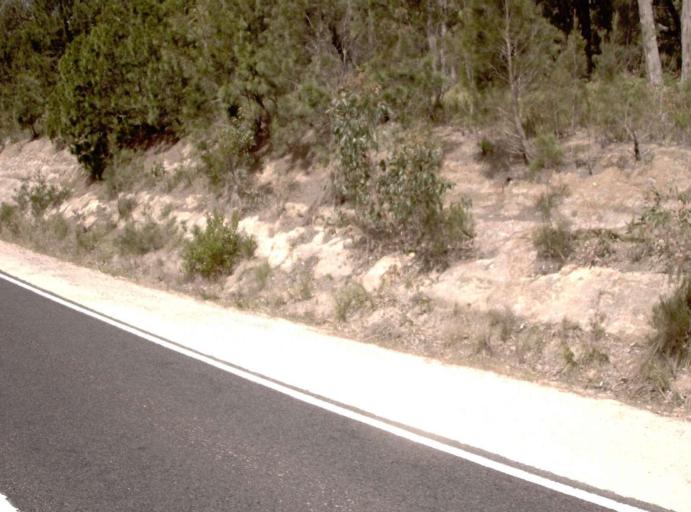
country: AU
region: New South Wales
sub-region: Bega Valley
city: Eden
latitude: -37.4223
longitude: 149.6475
